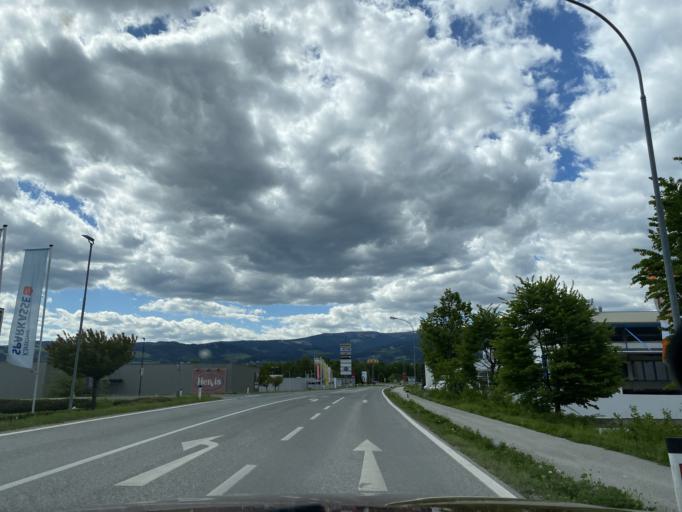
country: AT
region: Carinthia
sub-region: Politischer Bezirk Wolfsberg
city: Wolfsberg
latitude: 46.8186
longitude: 14.8400
